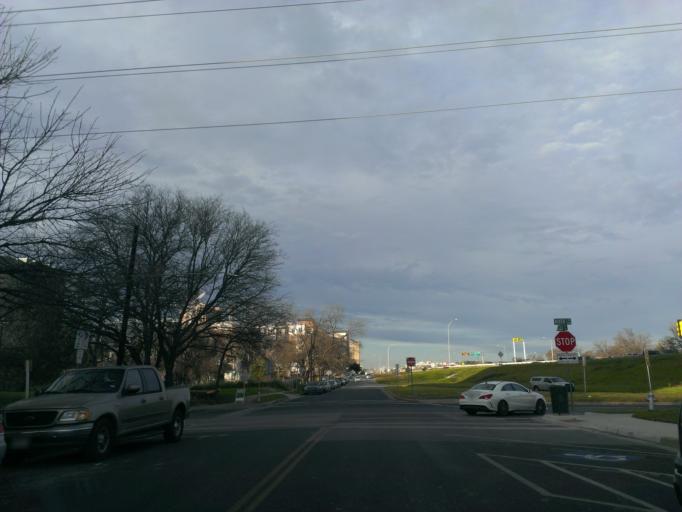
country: US
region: Texas
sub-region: Travis County
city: Austin
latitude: 30.2572
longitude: -97.7382
